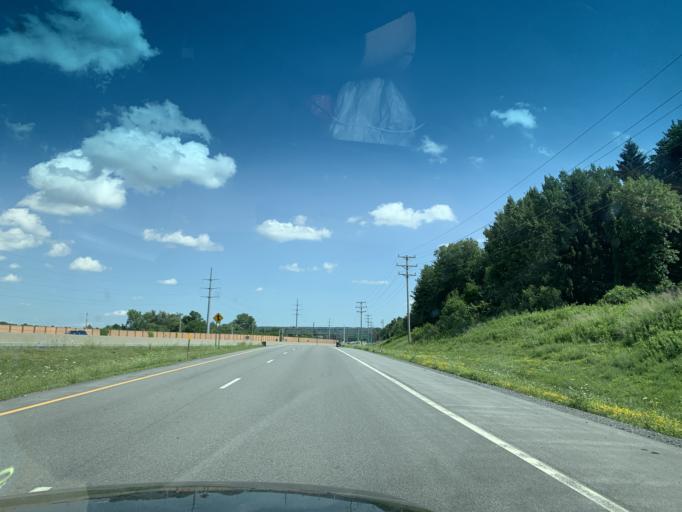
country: US
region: New York
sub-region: Oneida County
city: New York Mills
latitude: 43.0898
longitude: -75.3065
